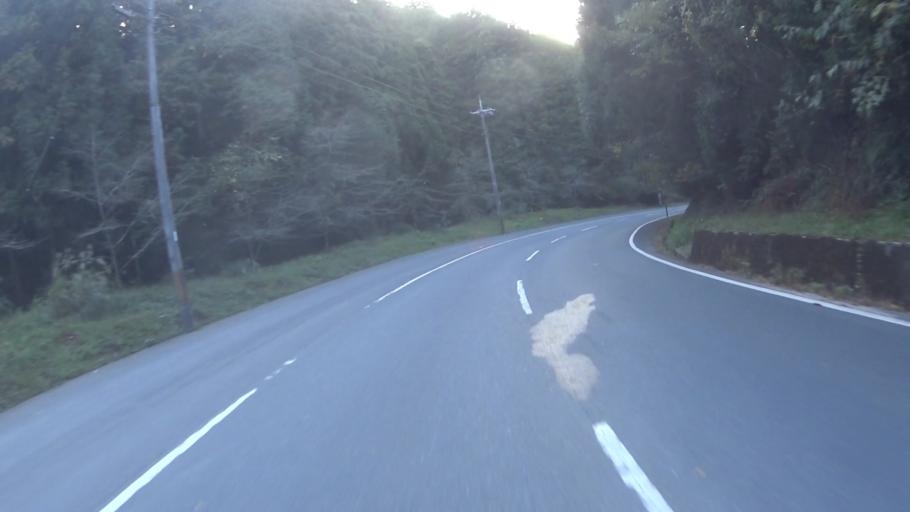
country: JP
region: Kyoto
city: Maizuru
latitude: 35.4644
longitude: 135.2472
